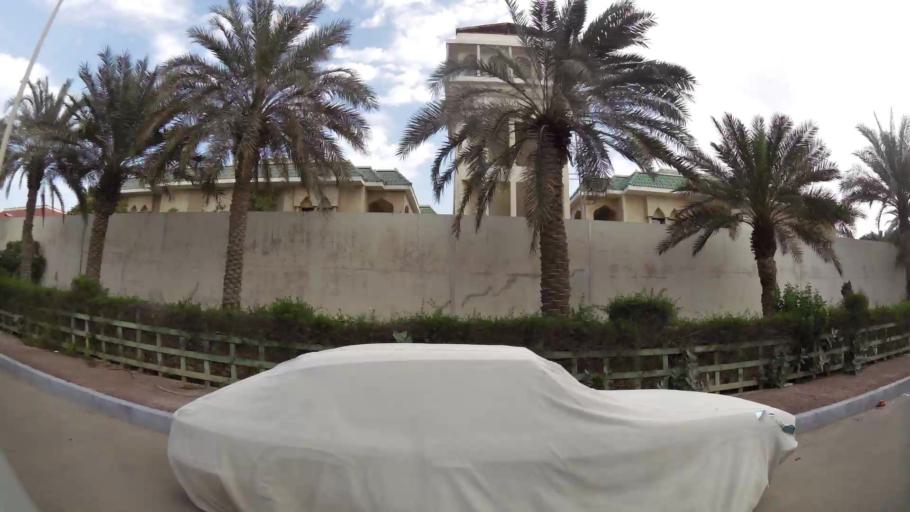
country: AE
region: Abu Dhabi
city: Abu Dhabi
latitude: 24.4520
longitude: 54.3528
